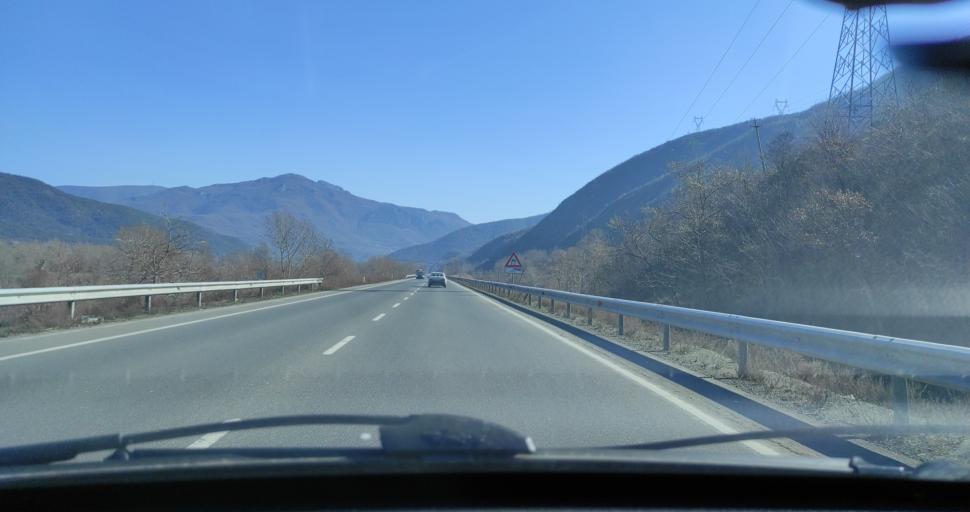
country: AL
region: Lezhe
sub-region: Rrethi i Kurbinit
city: Milot
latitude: 41.6982
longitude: 19.7409
